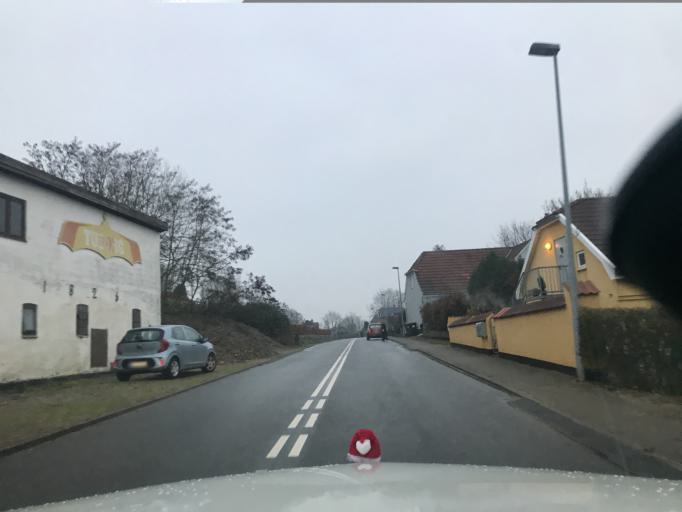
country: DK
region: South Denmark
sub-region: Sonderborg Kommune
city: Grasten
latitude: 54.8950
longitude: 9.5639
